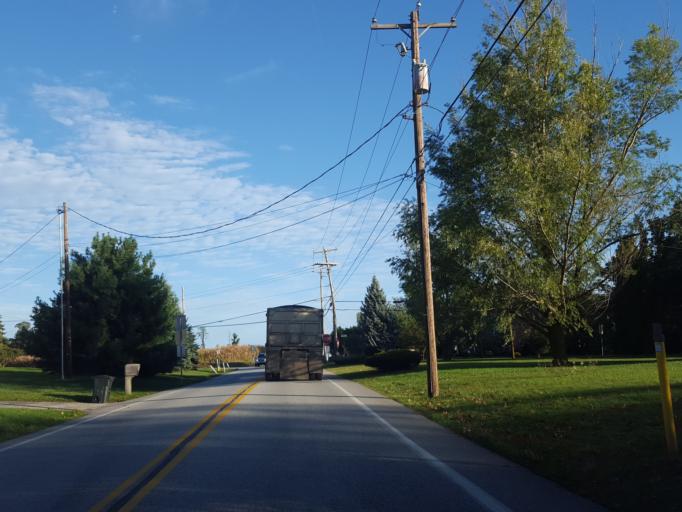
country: US
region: Pennsylvania
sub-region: York County
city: Stonybrook
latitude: 39.9709
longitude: -76.6151
